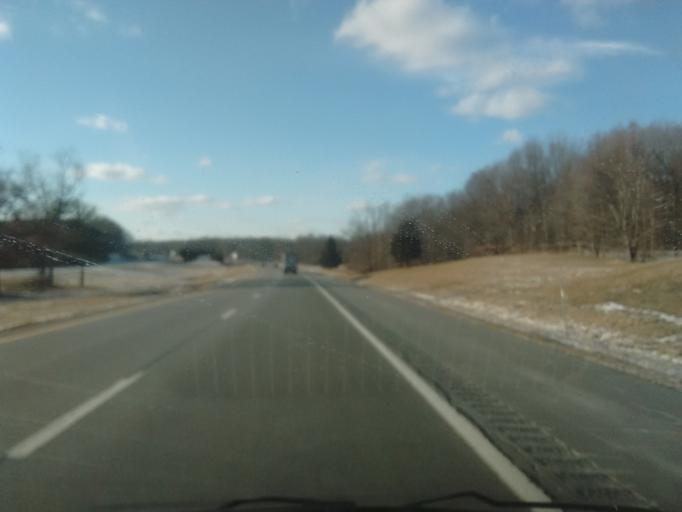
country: US
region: New York
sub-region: Orange County
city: Walden
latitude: 41.5160
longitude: -74.1634
